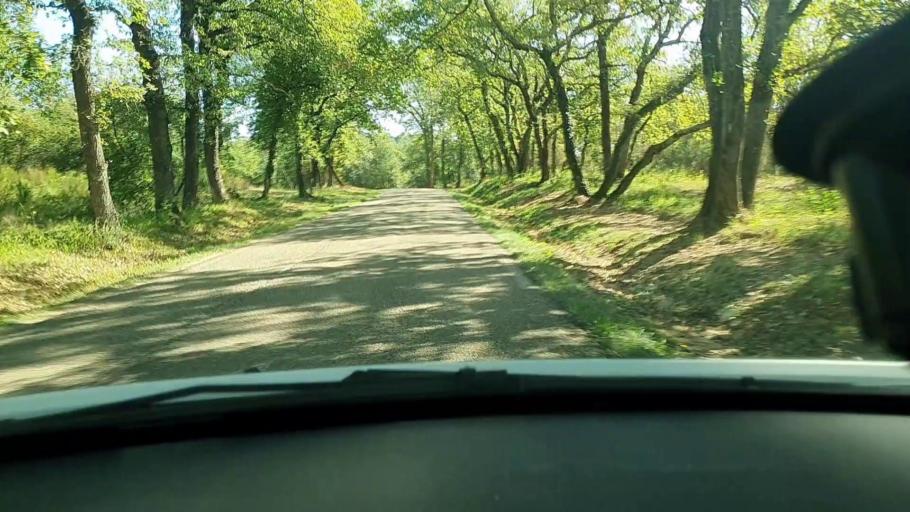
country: FR
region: Languedoc-Roussillon
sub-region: Departement du Gard
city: Saint-Julien-de-Peyrolas
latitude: 44.2784
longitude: 4.5412
